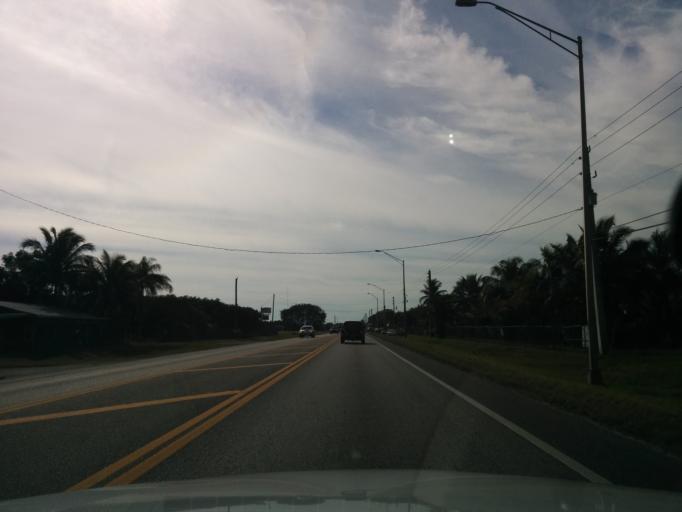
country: US
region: Florida
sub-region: Miami-Dade County
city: Richmond West
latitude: 25.6074
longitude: -80.4789
